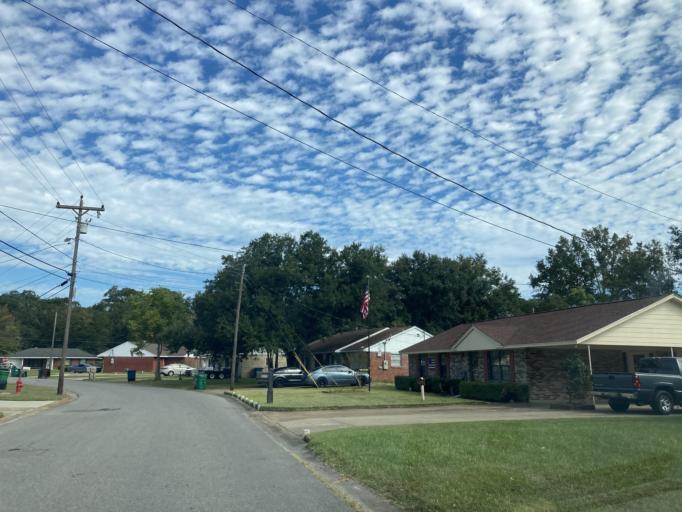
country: US
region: Mississippi
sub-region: Jackson County
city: Saint Martin
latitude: 30.4464
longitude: -88.8723
